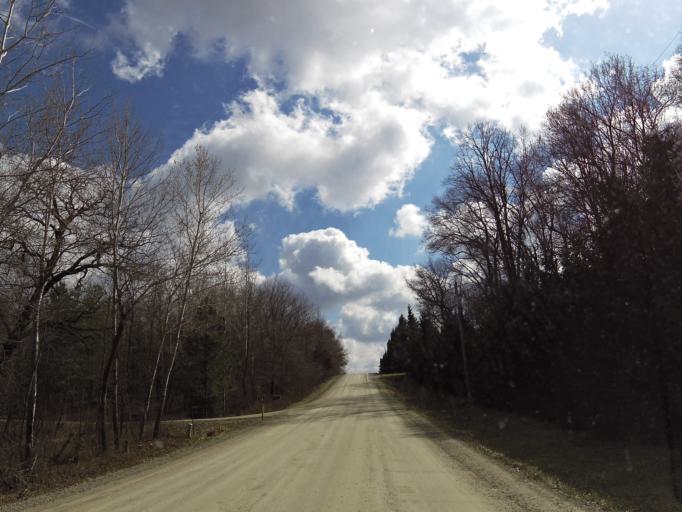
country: US
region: Minnesota
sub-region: Dodge County
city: Mantorville
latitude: 44.0745
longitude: -92.7183
